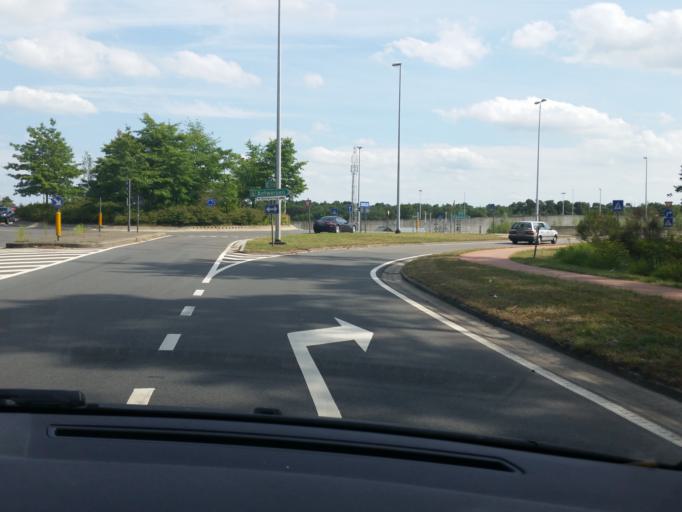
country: BE
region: Flanders
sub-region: Provincie Antwerpen
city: Brasschaat
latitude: 51.3109
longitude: 4.5543
